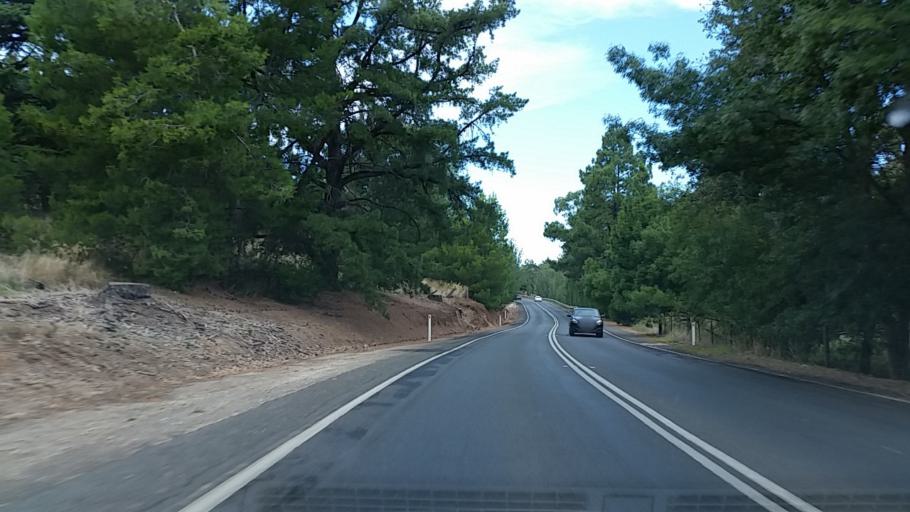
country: AU
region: South Australia
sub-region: Barossa
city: Angaston
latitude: -34.4963
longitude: 139.0348
